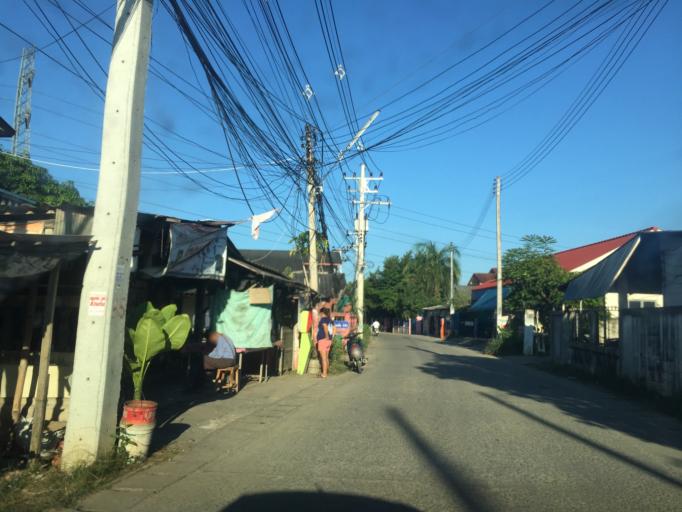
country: TH
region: Lamphun
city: Lamphun
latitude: 18.5984
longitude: 99.0523
